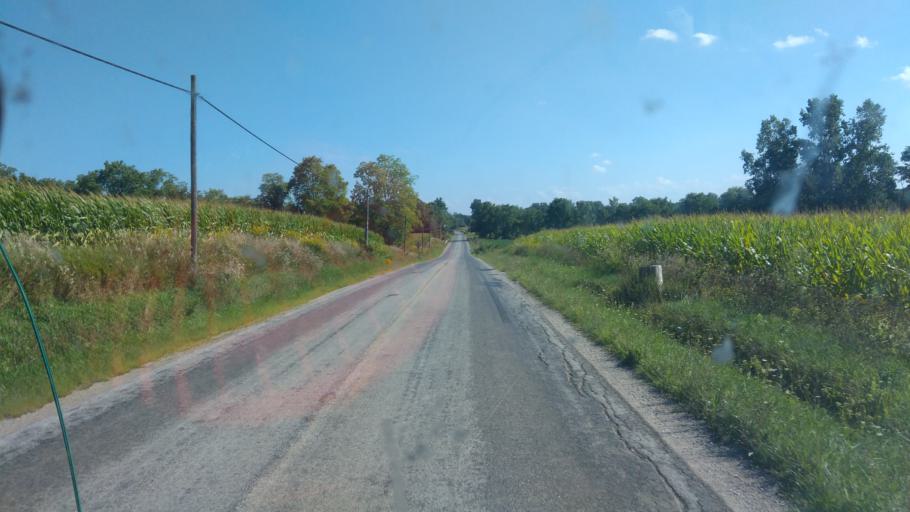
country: US
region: Ohio
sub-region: Ashland County
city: Ashland
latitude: 40.8939
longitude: -82.4294
